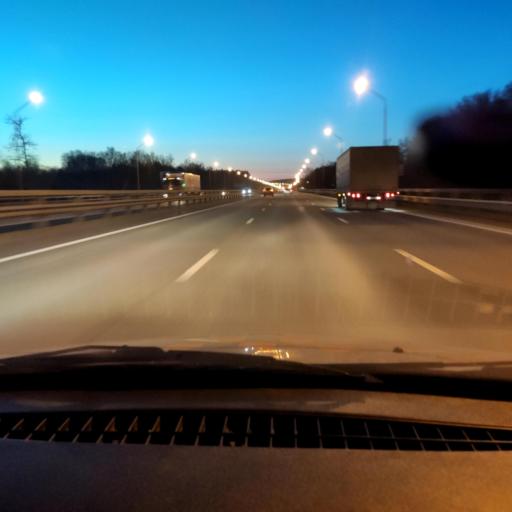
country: RU
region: Bashkortostan
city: Avdon
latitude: 54.6688
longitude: 55.8472
